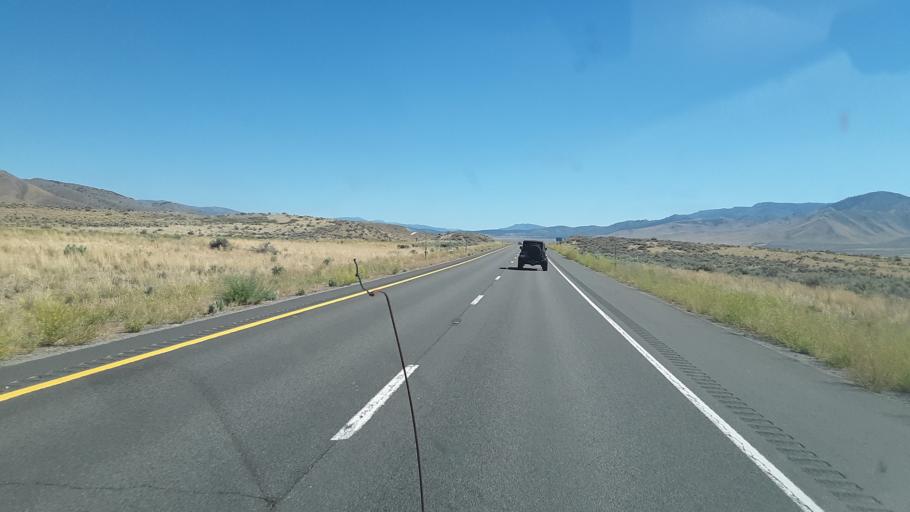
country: US
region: Nevada
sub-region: Washoe County
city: Cold Springs
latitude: 39.7543
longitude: -120.0395
